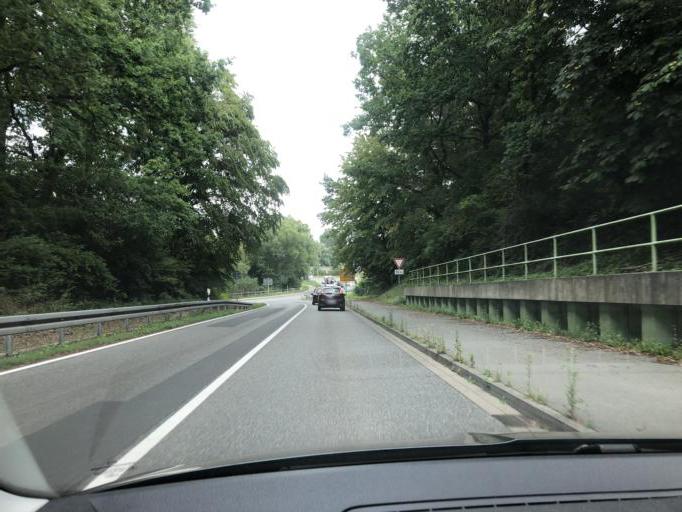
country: DE
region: Mecklenburg-Vorpommern
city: Neumuehle
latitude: 53.6235
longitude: 11.3583
